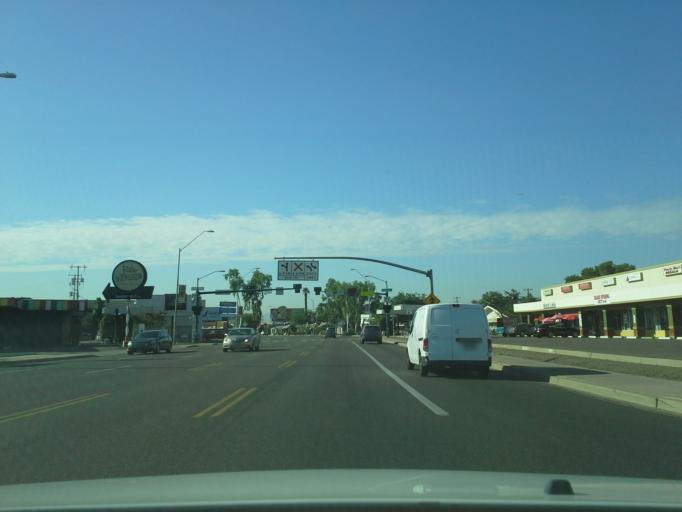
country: US
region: Arizona
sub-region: Maricopa County
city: Phoenix
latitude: 33.4994
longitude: -112.0829
